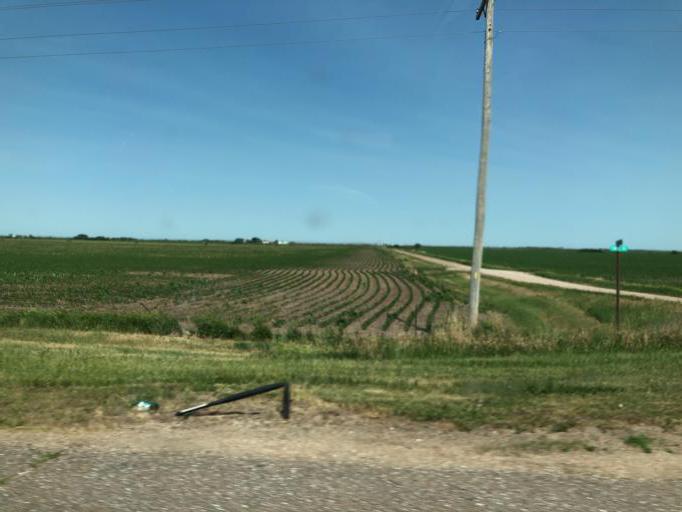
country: US
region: Nebraska
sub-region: Fillmore County
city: Geneva
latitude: 40.4660
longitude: -97.5959
